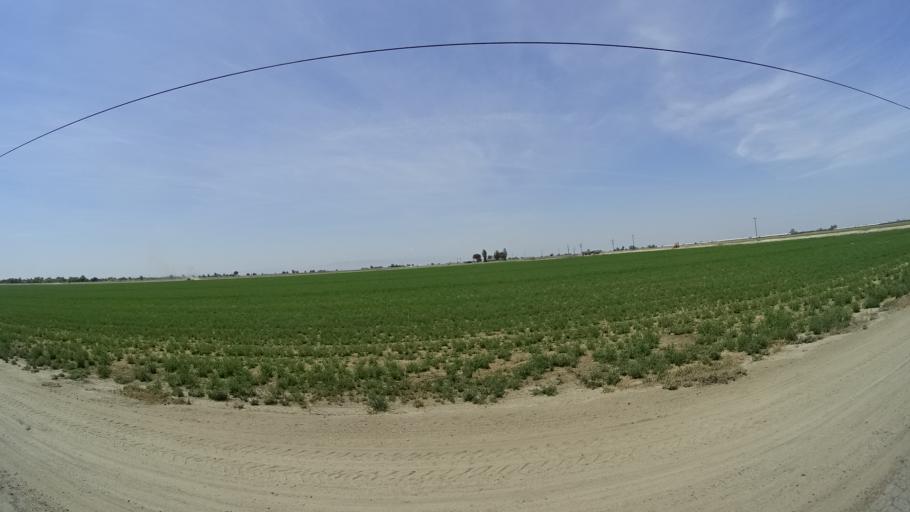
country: US
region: California
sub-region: Fresno County
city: Riverdale
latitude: 36.4006
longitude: -119.9051
